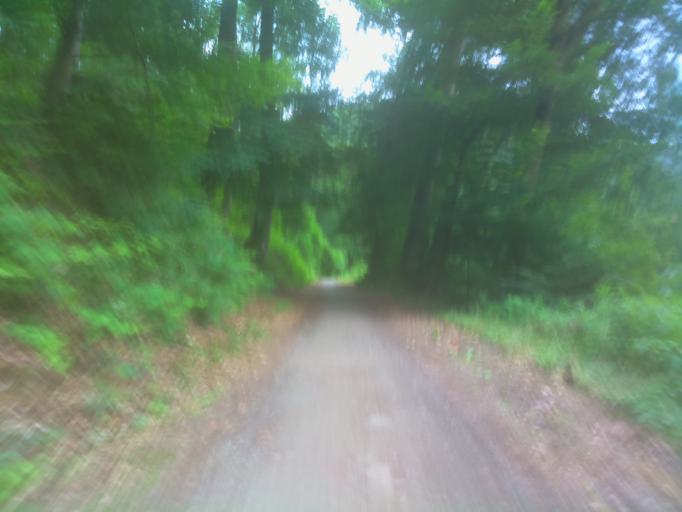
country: DE
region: Hesse
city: Neckarsteinach
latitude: 49.3971
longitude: 8.8566
